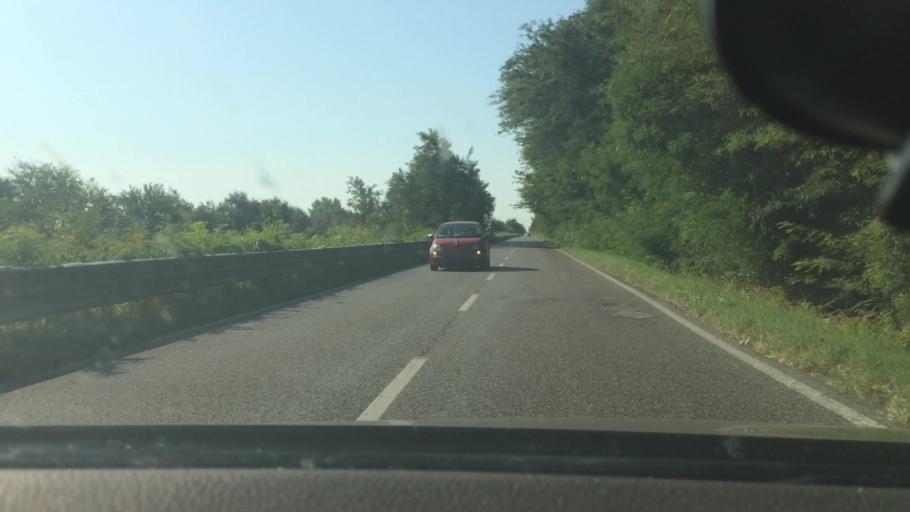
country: IT
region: Emilia-Romagna
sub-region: Provincia di Ferrara
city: Lagosanto
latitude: 44.7429
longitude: 12.1424
